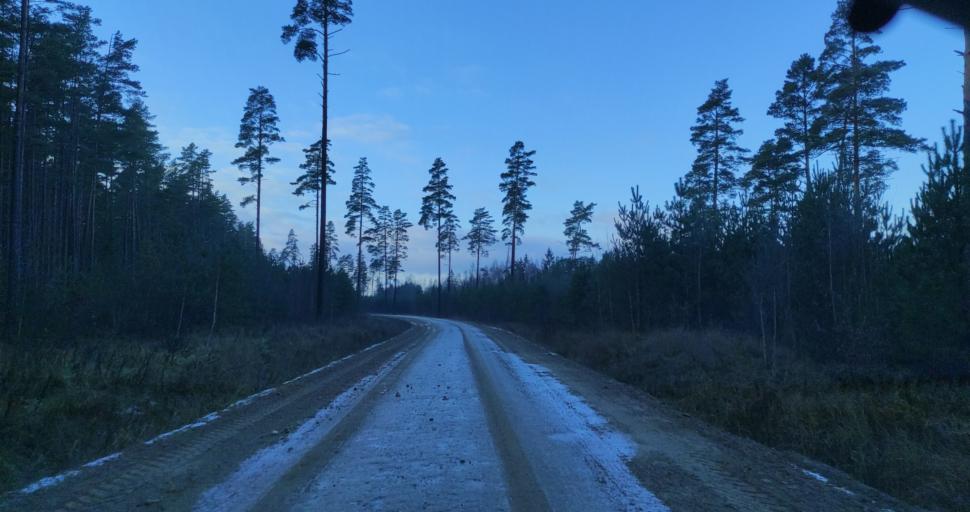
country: LV
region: Kuldigas Rajons
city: Kuldiga
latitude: 57.0532
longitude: 21.8369
